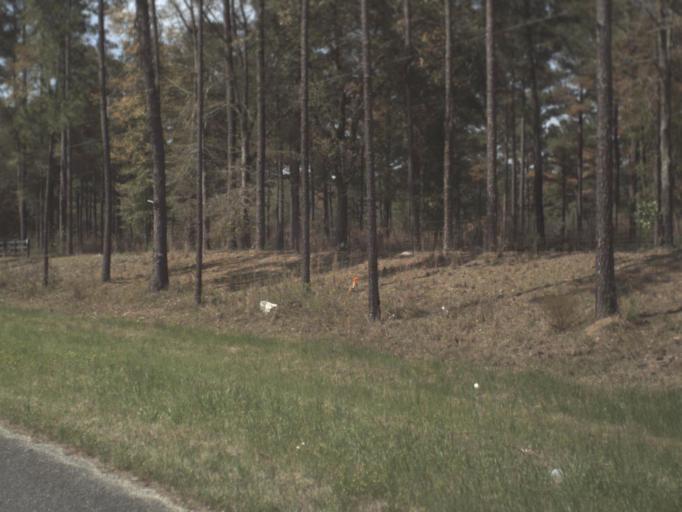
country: US
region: Florida
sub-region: Gadsden County
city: Midway
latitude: 30.5528
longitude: -84.5022
